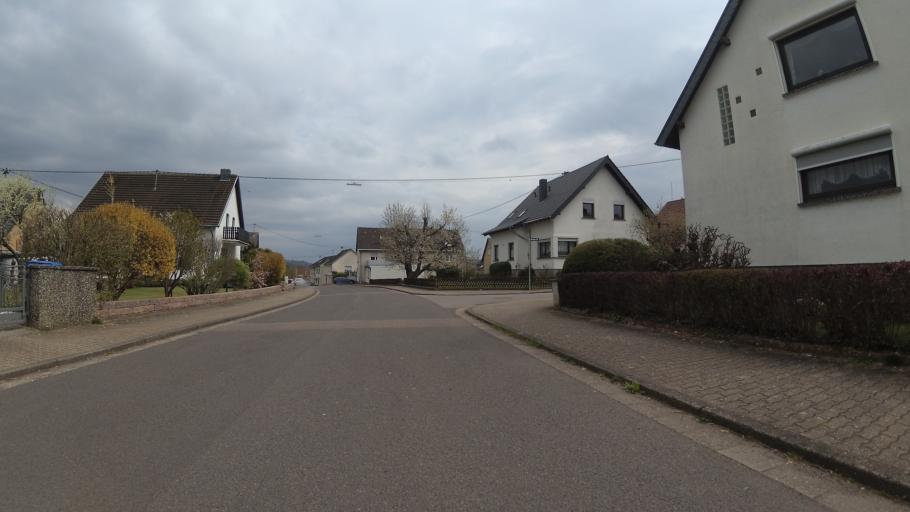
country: DE
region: Saarland
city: Merzig
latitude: 49.4325
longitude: 6.6175
